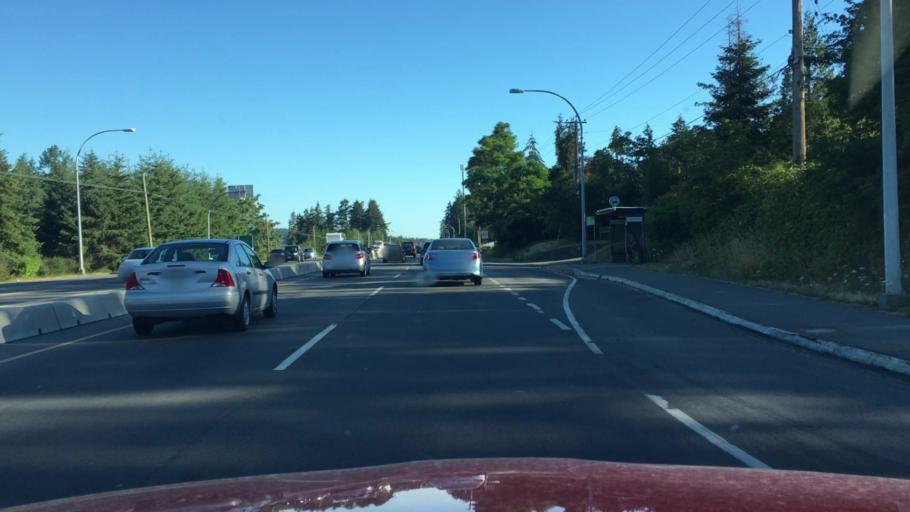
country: CA
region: British Columbia
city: Victoria
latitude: 48.5146
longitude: -123.3843
